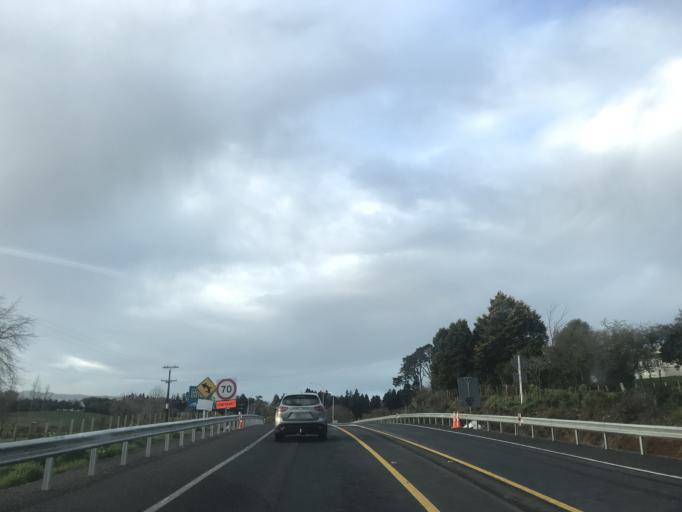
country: NZ
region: Waikato
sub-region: Hauraki District
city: Waihi
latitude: -37.4372
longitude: 175.8731
